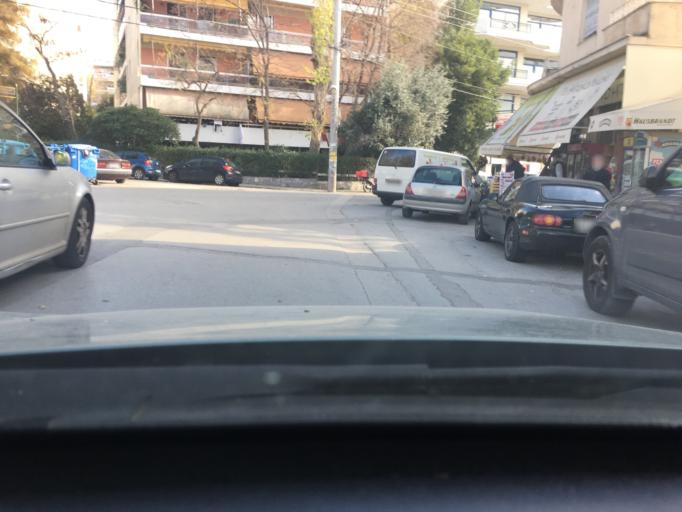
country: GR
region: Attica
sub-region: Nomarchia Athinas
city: Khalandrion
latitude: 38.0265
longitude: 23.7998
